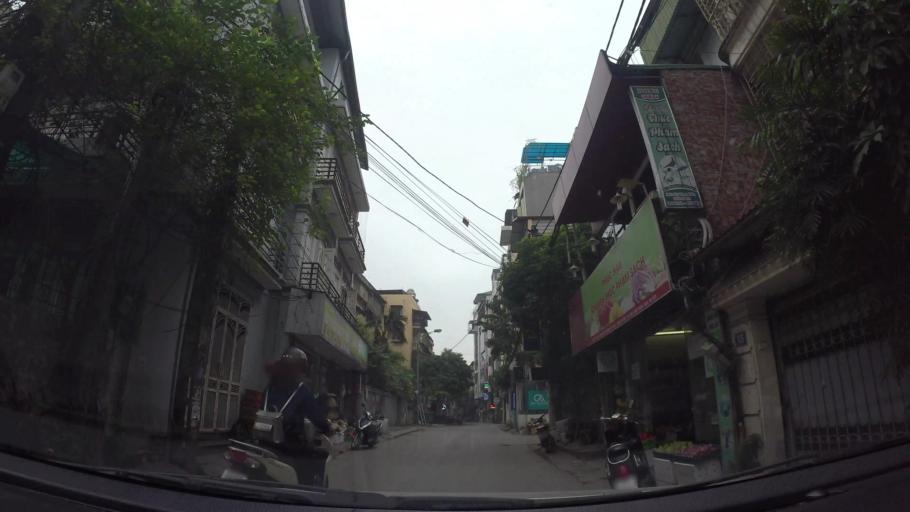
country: VN
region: Ha Noi
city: Cau Giay
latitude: 21.0339
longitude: 105.8172
